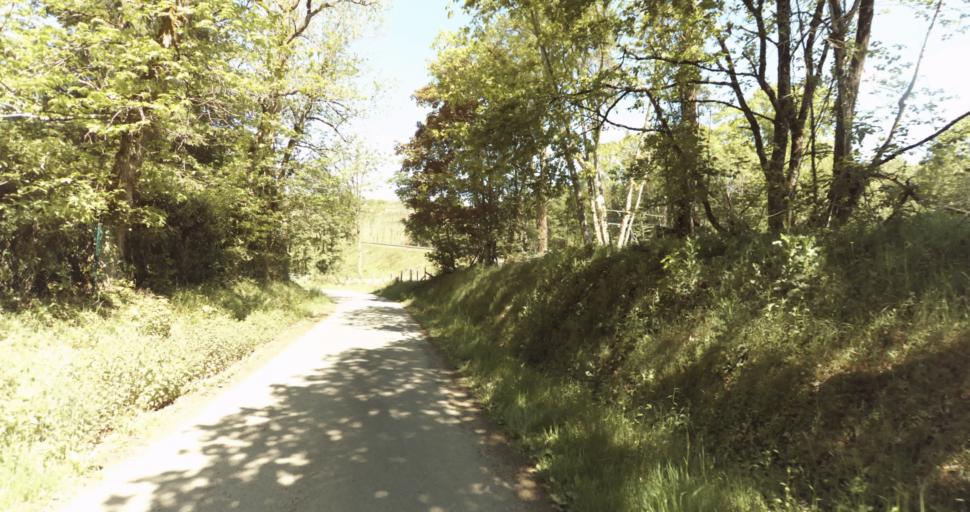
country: FR
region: Limousin
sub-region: Departement de la Haute-Vienne
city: Le Vigen
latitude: 45.7496
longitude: 1.3076
